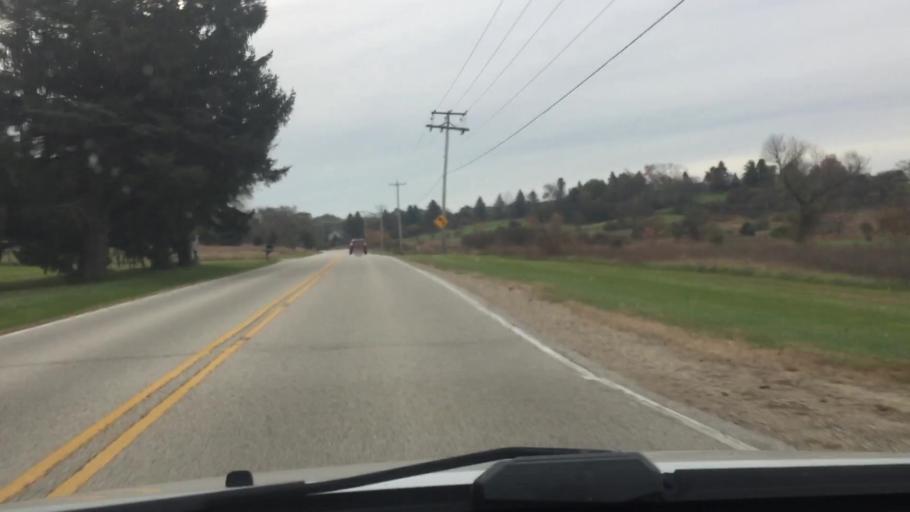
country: US
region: Wisconsin
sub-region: Waukesha County
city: Mukwonago
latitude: 42.8865
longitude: -88.3758
